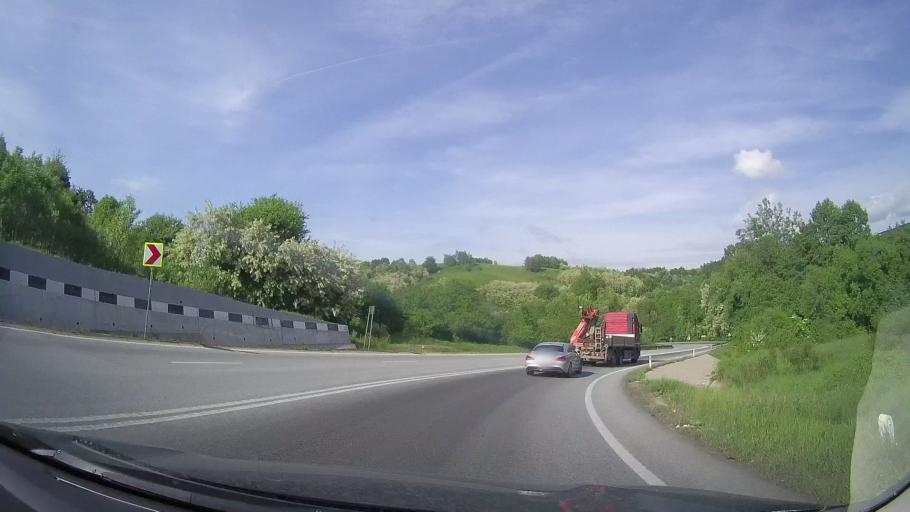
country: RO
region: Caras-Severin
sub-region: Comuna Domasnea
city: Domasnea
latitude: 45.1048
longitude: 22.3114
